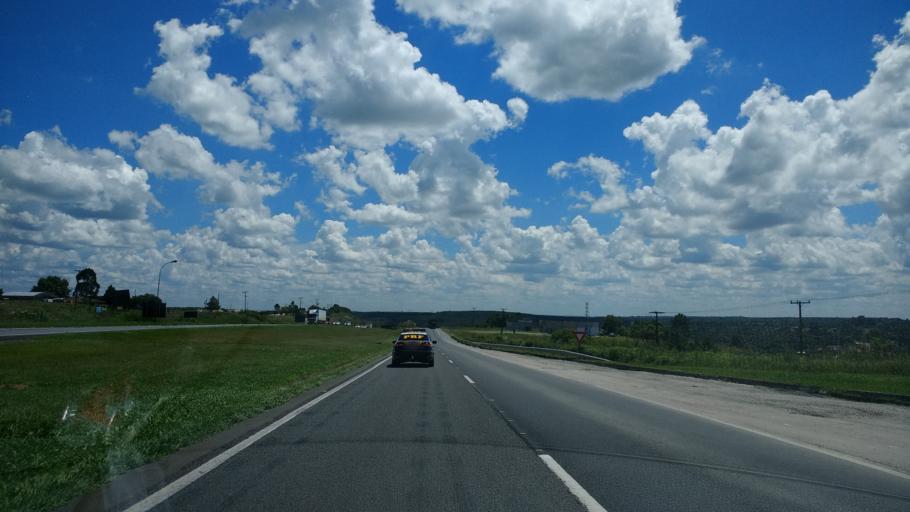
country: BR
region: Parana
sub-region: Campo Largo
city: Campo Largo
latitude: -25.4741
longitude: -49.7040
